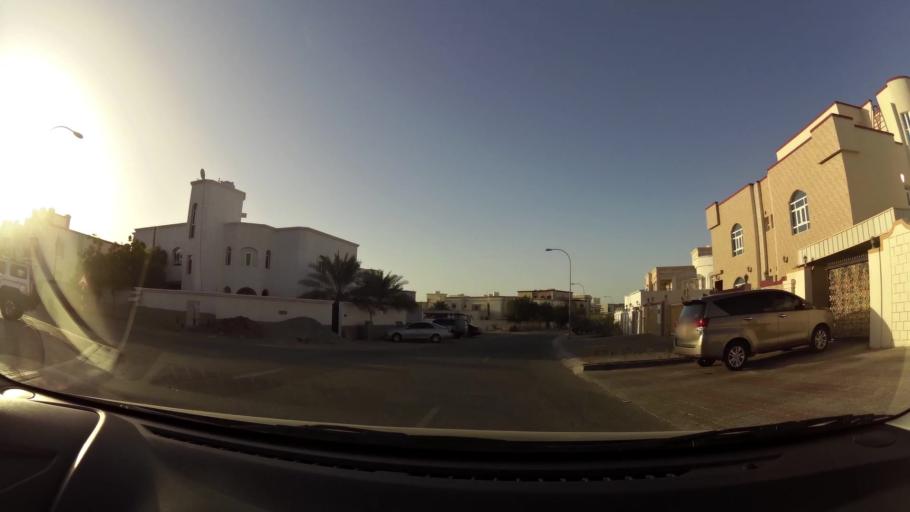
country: OM
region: Muhafazat Masqat
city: As Sib al Jadidah
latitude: 23.6057
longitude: 58.2229
